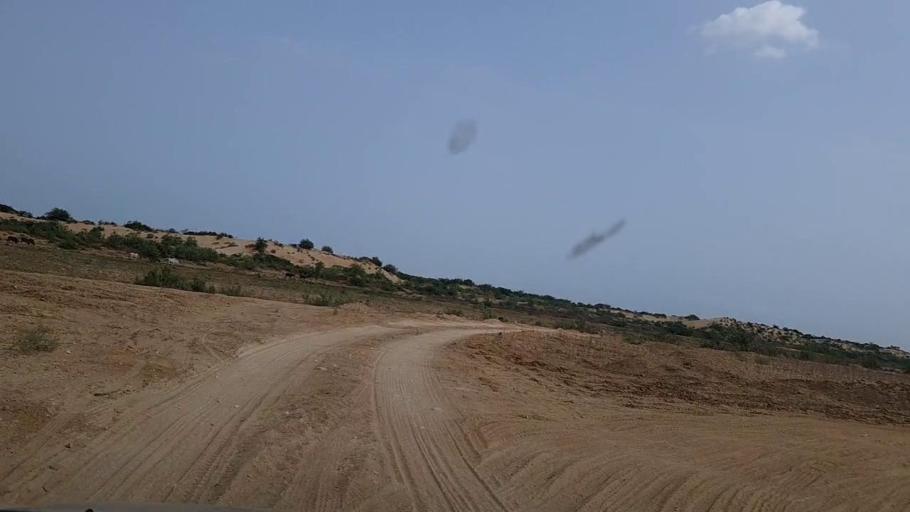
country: PK
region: Sindh
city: Kotri
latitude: 25.2693
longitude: 68.2673
